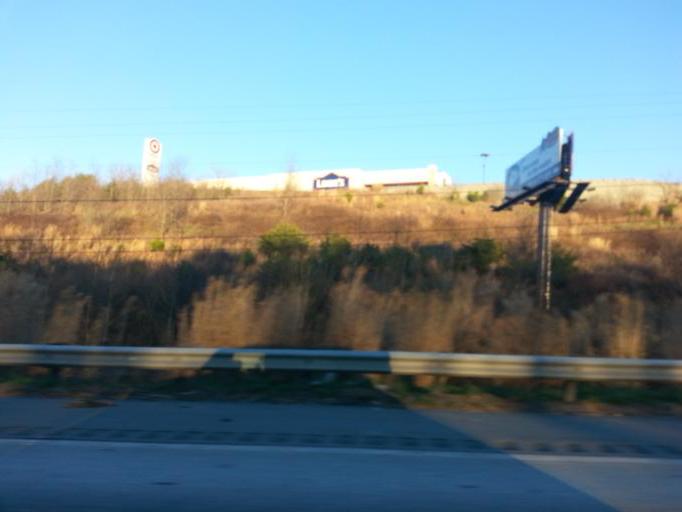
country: US
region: North Carolina
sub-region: Buncombe County
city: Royal Pines
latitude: 35.4483
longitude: -82.5405
